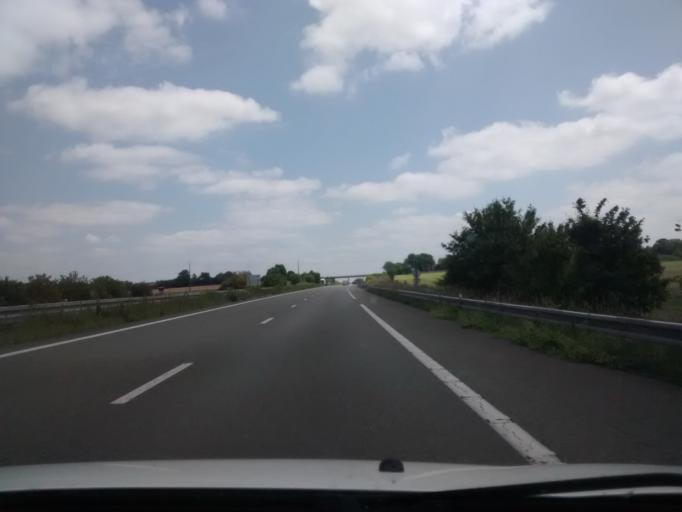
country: FR
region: Pays de la Loire
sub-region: Departement de la Mayenne
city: Bonchamp-les-Laval
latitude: 48.0912
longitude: -0.6813
